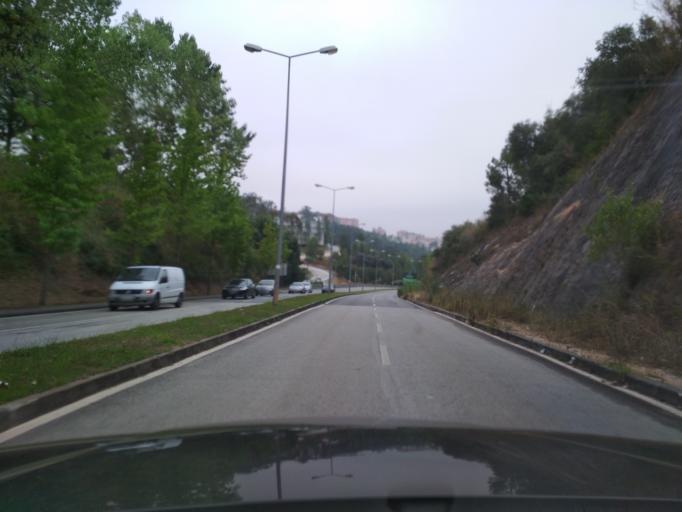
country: PT
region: Coimbra
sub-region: Coimbra
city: Coimbra
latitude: 40.2225
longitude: -8.4153
